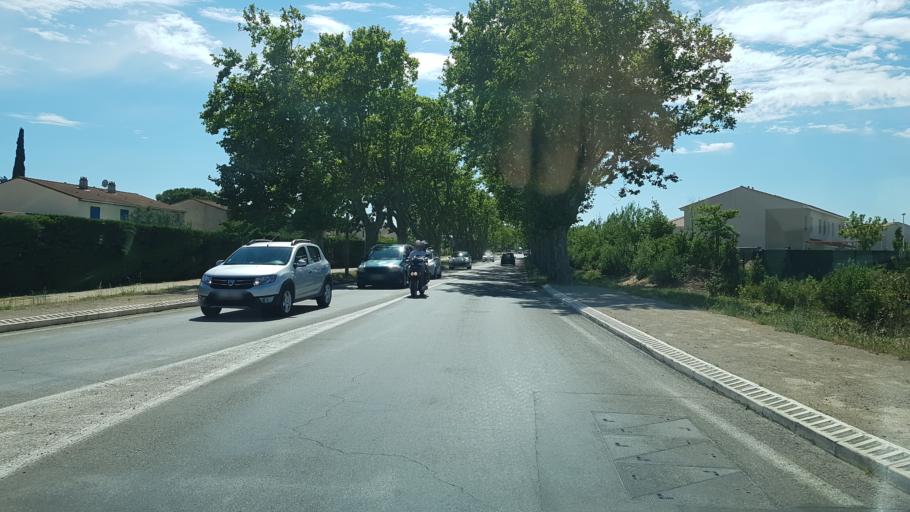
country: FR
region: Provence-Alpes-Cote d'Azur
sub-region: Departement des Bouches-du-Rhone
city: Saint-Martin-de-Crau
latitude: 43.6372
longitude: 4.7983
